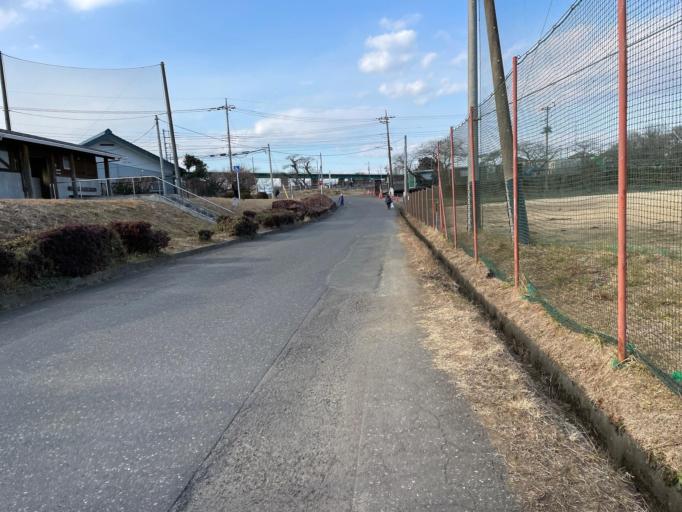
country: JP
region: Saitama
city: Hanno
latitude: 35.8358
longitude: 139.3352
